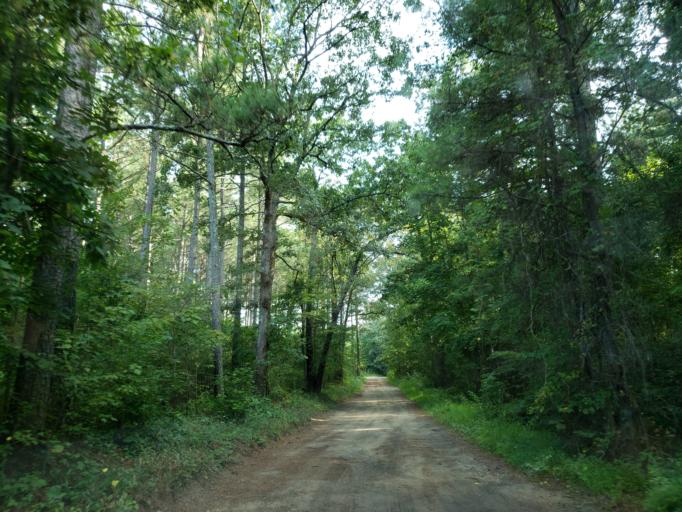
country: US
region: Georgia
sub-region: Cobb County
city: Acworth
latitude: 34.1840
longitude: -84.6460
